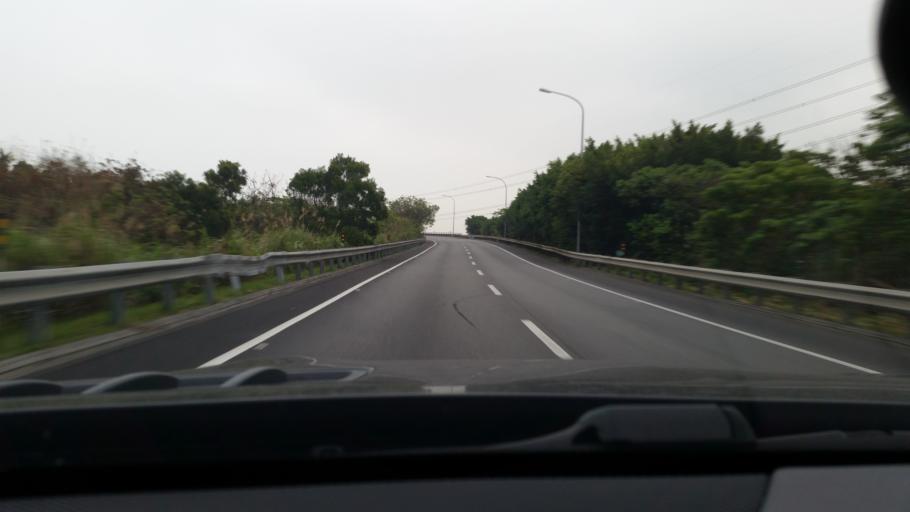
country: TW
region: Taiwan
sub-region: Taoyuan
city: Taoyuan
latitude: 24.9376
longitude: 121.3214
